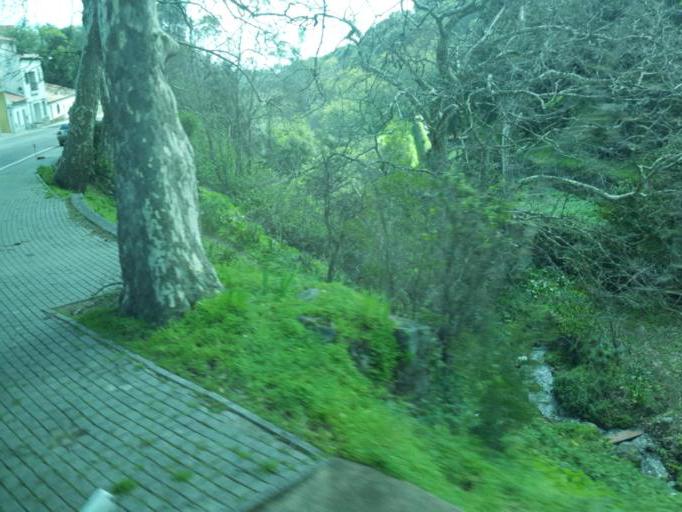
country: PT
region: Faro
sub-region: Monchique
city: Monchique
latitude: 37.2891
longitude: -8.5543
